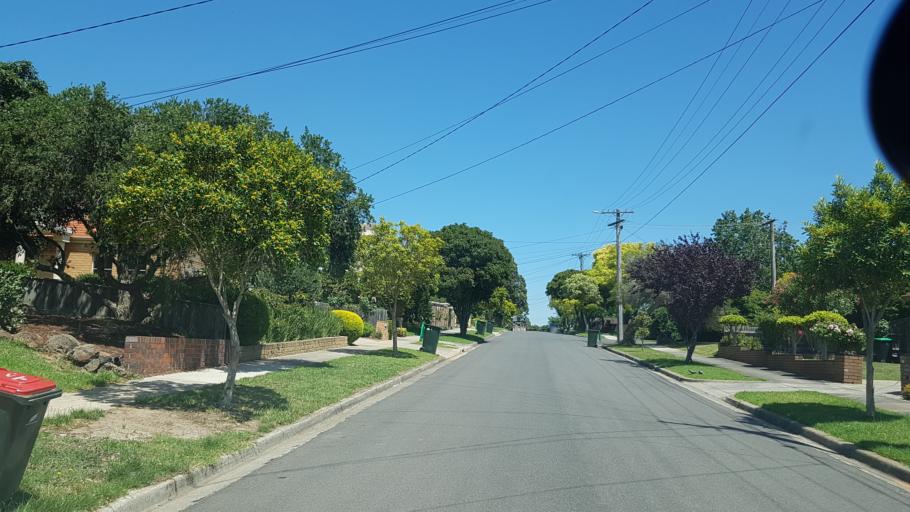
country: AU
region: Victoria
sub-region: Manningham
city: Bulleen
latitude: -37.7568
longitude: 145.0952
